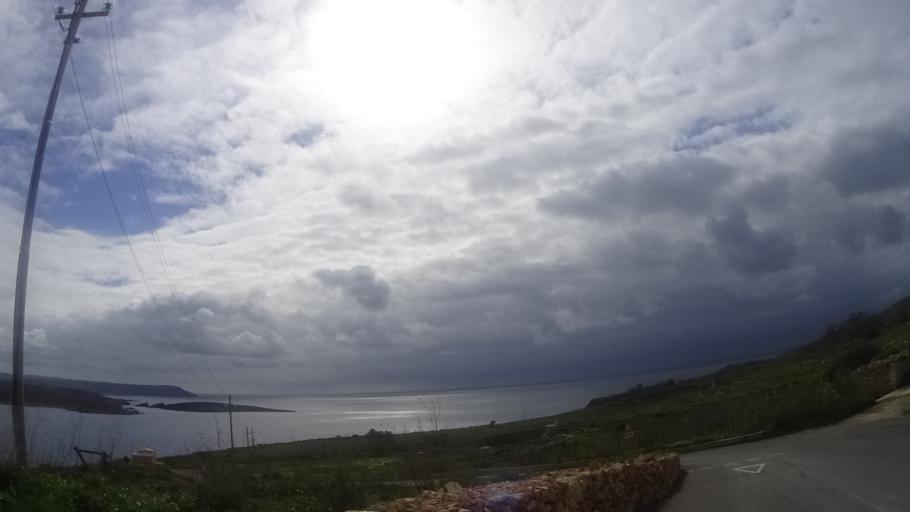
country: MT
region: Il-Qala
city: Qala
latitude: 36.0309
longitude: 14.3212
